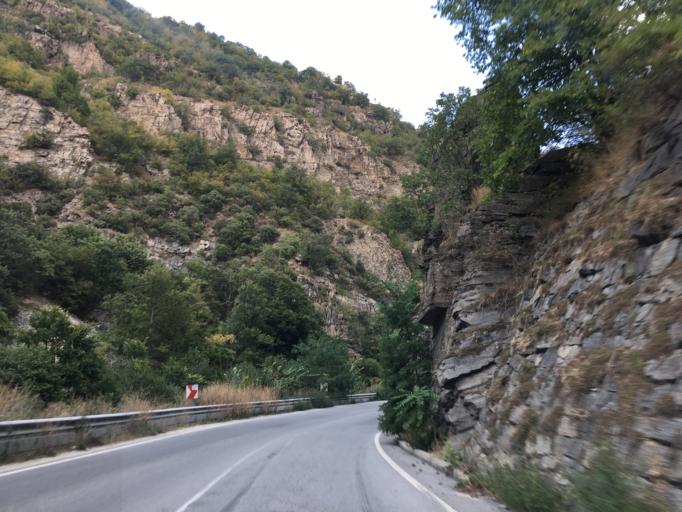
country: BG
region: Pazardzhik
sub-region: Obshtina Septemvri
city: Septemvri
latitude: 42.1376
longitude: 24.1250
